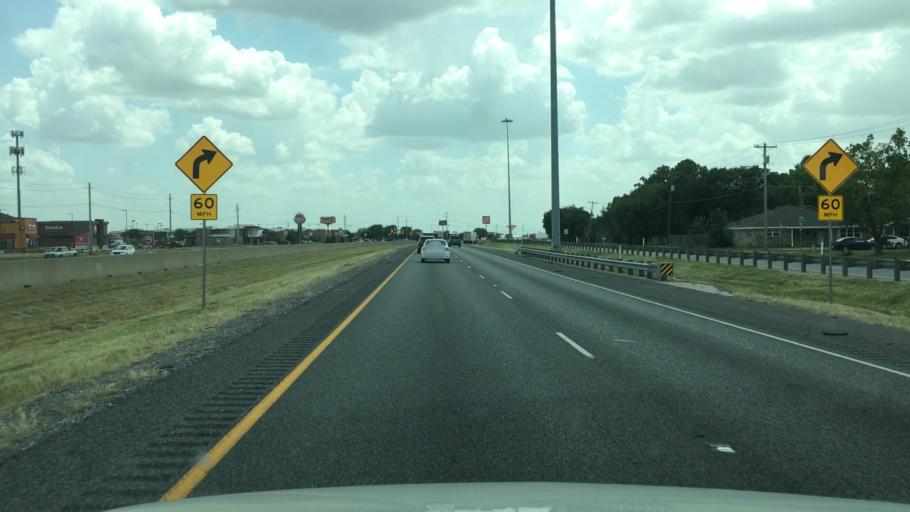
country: US
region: Texas
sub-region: Hunt County
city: Greenville
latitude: 33.1029
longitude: -96.1039
